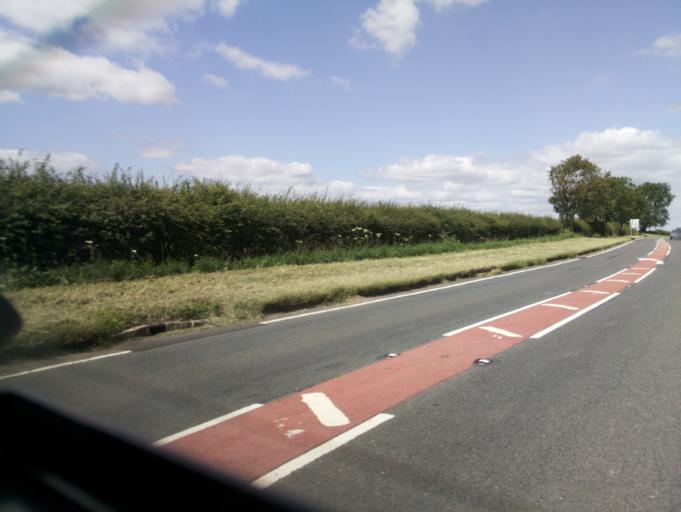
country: GB
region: England
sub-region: Buckinghamshire
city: Aylesbury
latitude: 51.8495
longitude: -0.8263
